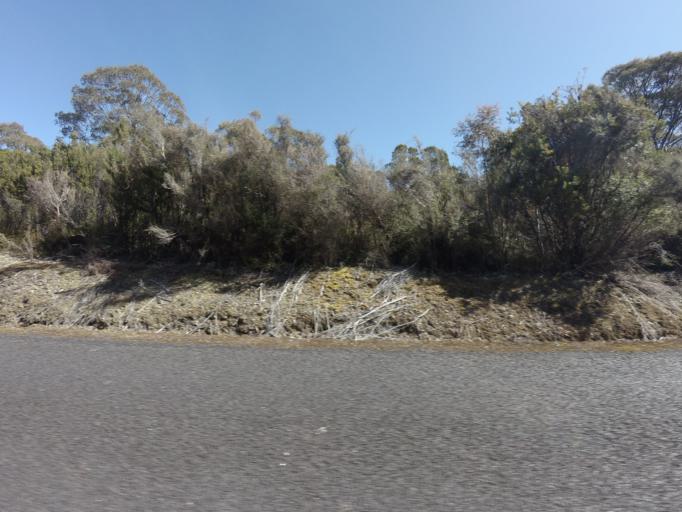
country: AU
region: Tasmania
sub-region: Derwent Valley
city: New Norfolk
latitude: -42.7615
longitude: 146.5328
